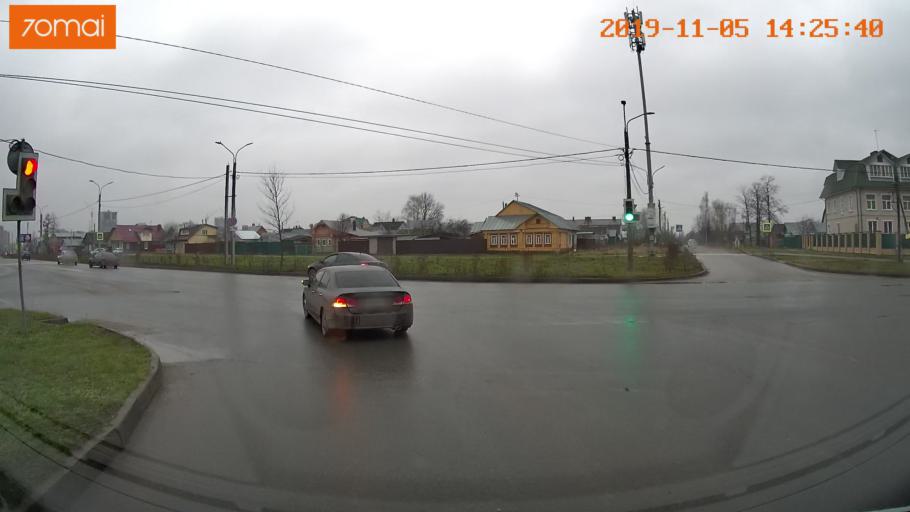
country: RU
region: Ivanovo
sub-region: Gorod Ivanovo
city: Ivanovo
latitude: 56.9713
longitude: 40.9932
